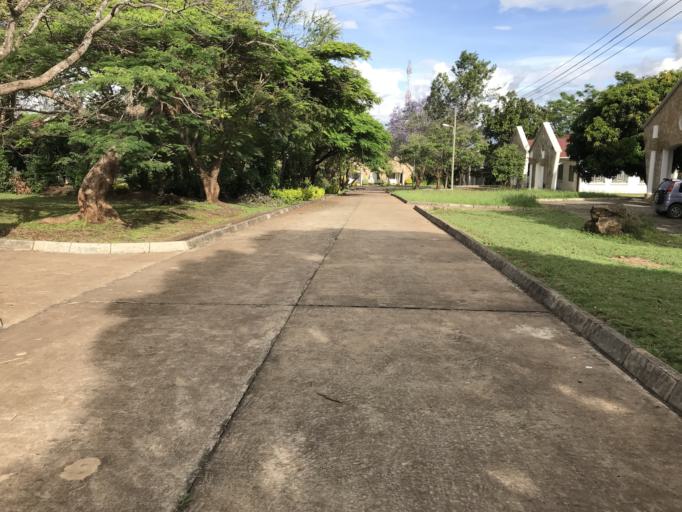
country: TZ
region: Arusha
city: Usa River
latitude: -3.3997
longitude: 36.8001
